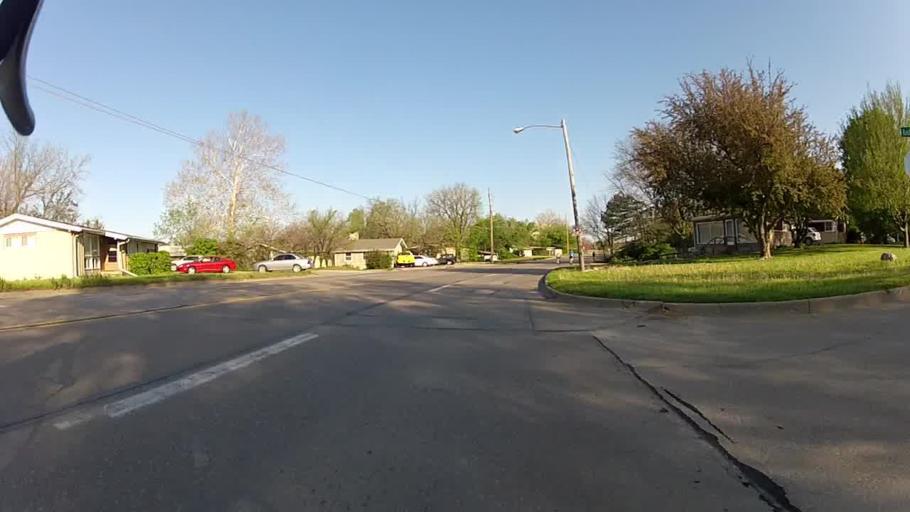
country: US
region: Kansas
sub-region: Riley County
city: Manhattan
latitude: 39.1865
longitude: -96.5967
